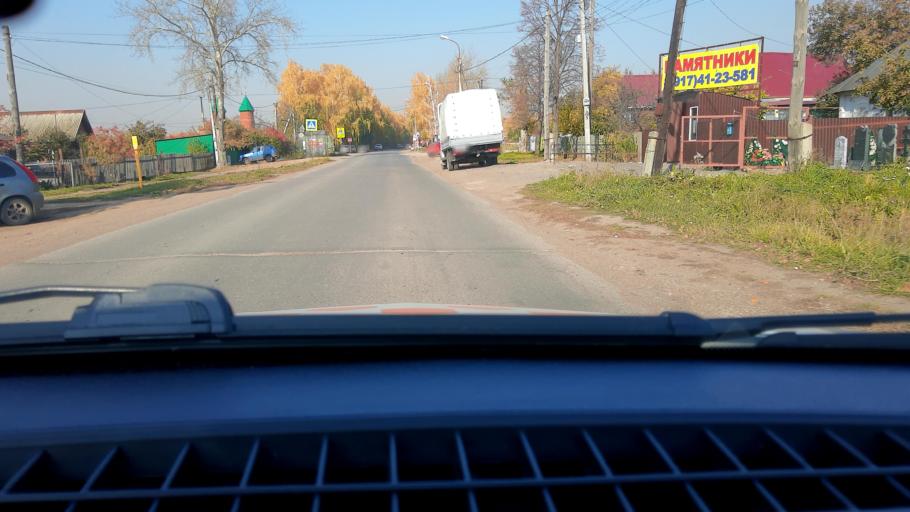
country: RU
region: Bashkortostan
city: Ufa
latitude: 54.8458
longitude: 56.1527
